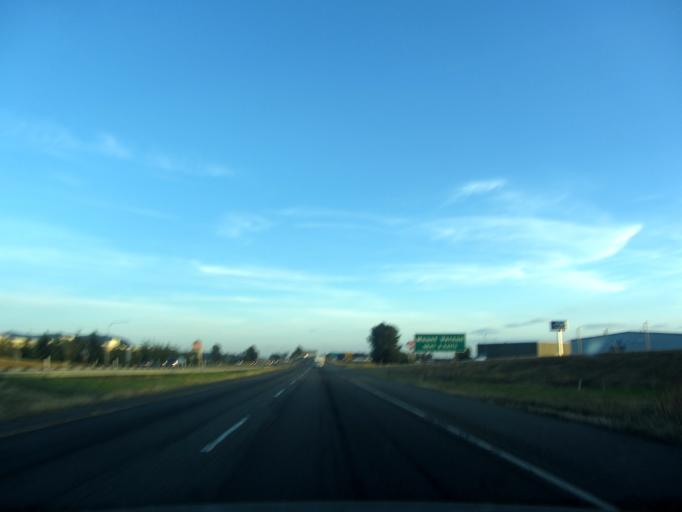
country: US
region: Washington
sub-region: Skagit County
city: Burlington
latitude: 48.4517
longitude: -122.3415
